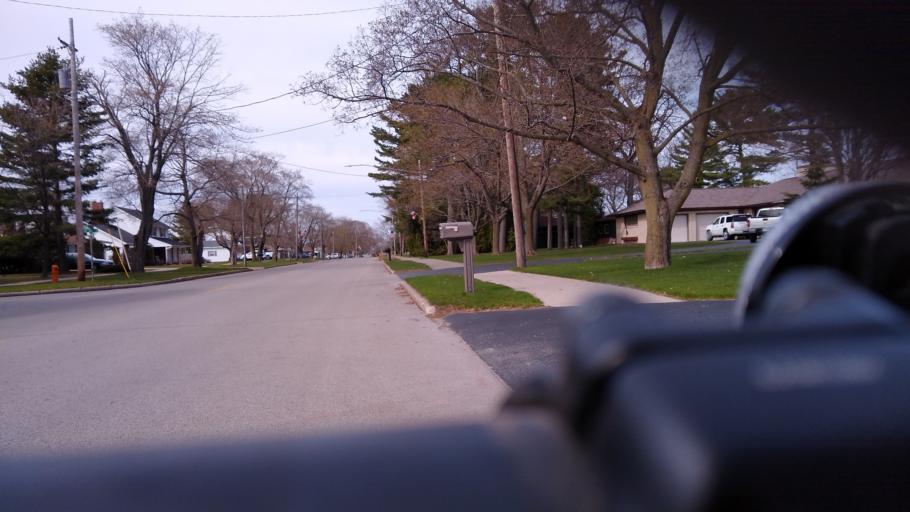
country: US
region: Michigan
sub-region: Delta County
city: Escanaba
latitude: 45.7256
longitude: -87.0673
